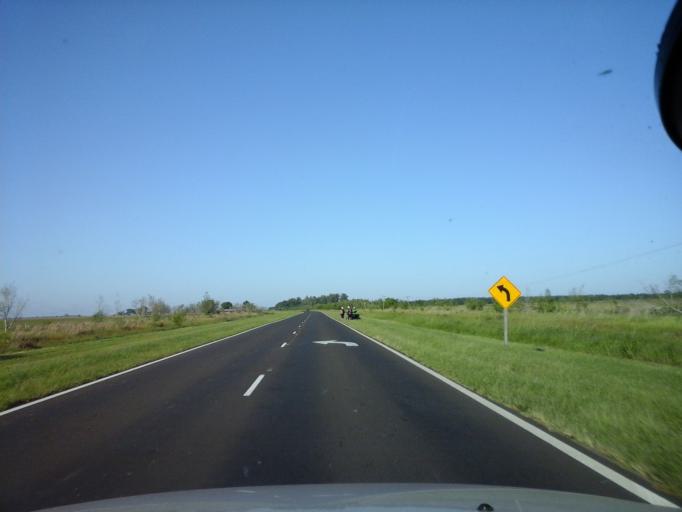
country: AR
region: Corrientes
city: Ita Ibate
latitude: -27.4452
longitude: -57.3868
